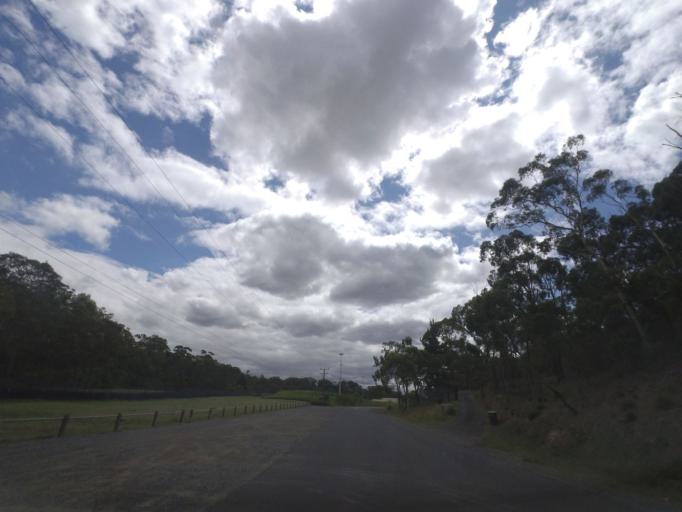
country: AU
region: Victoria
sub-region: Manningham
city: Park Orchards
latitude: -37.7704
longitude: 145.2060
